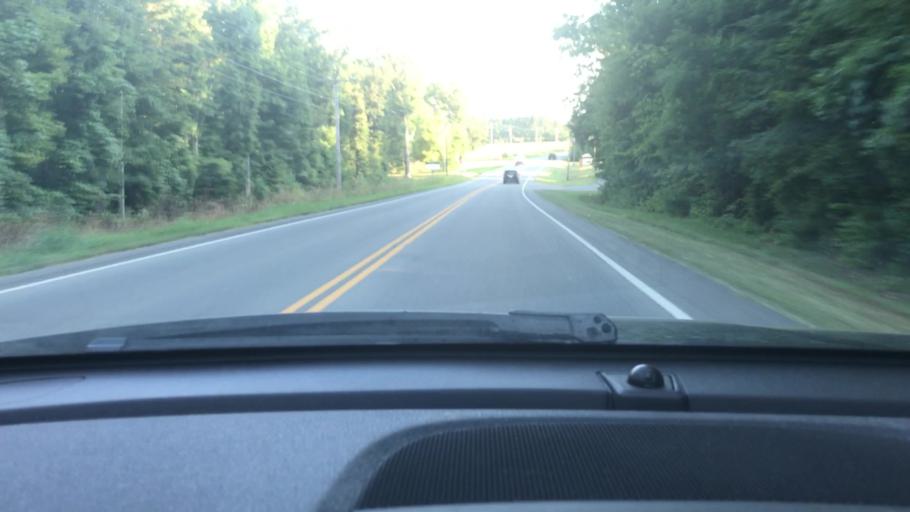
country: US
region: Tennessee
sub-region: Dickson County
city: Charlotte
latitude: 36.1496
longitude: -87.3560
